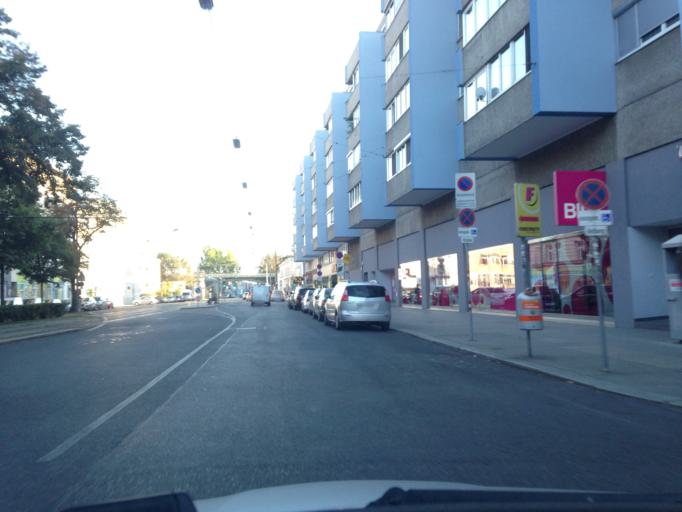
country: AT
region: Vienna
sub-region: Wien Stadt
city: Vienna
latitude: 48.2458
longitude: 16.3617
